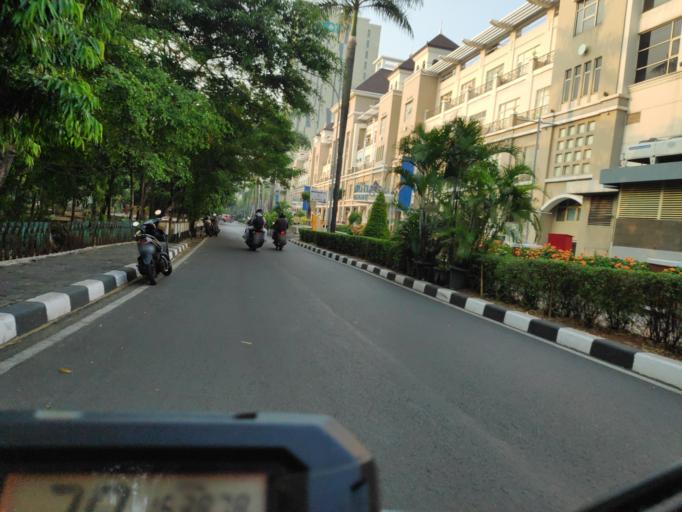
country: ID
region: Jakarta Raya
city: Jakarta
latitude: -6.2525
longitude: 106.8018
